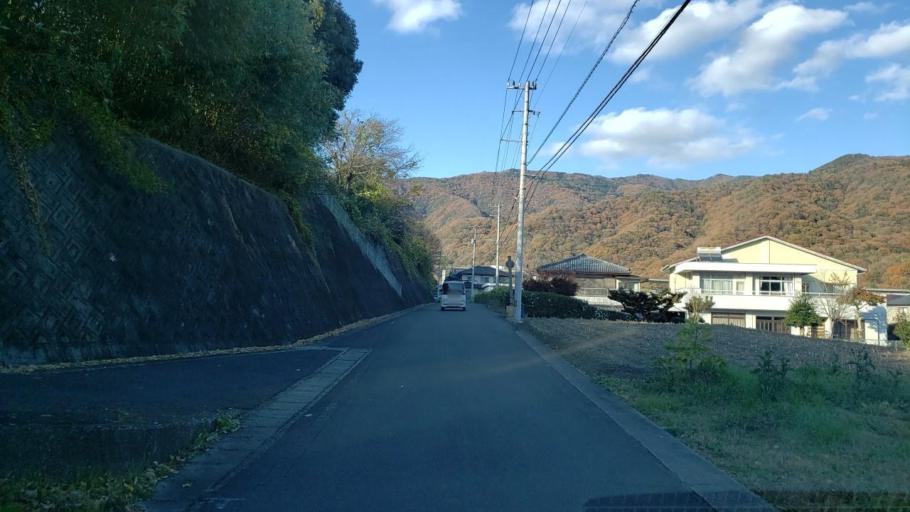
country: JP
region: Tokushima
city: Wakimachi
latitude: 34.0653
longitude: 134.0875
